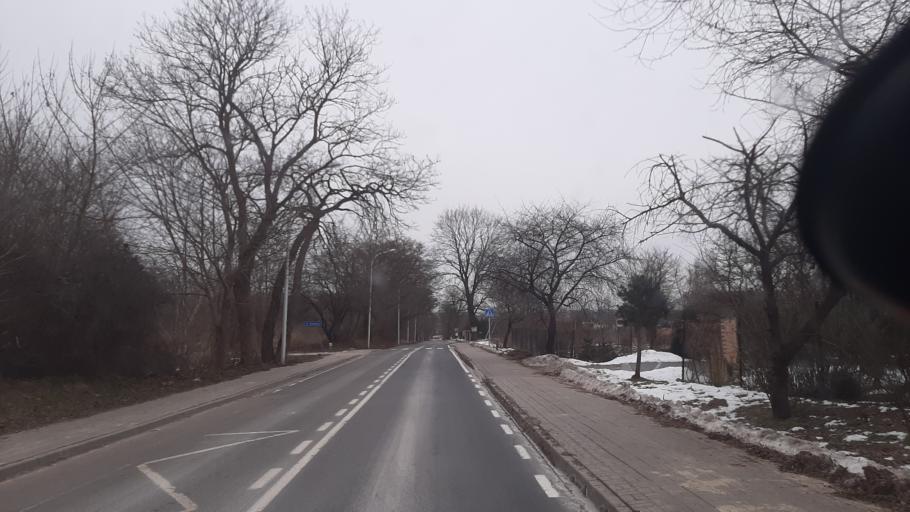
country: PL
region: Lublin Voivodeship
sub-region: Powiat lubelski
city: Lublin
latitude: 51.2789
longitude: 22.5941
